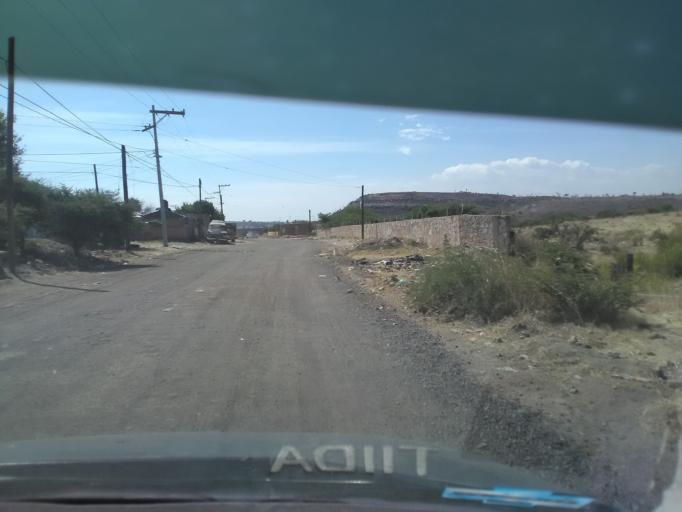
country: MX
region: Durango
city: Victoria de Durango
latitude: 24.0313
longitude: -104.7122
